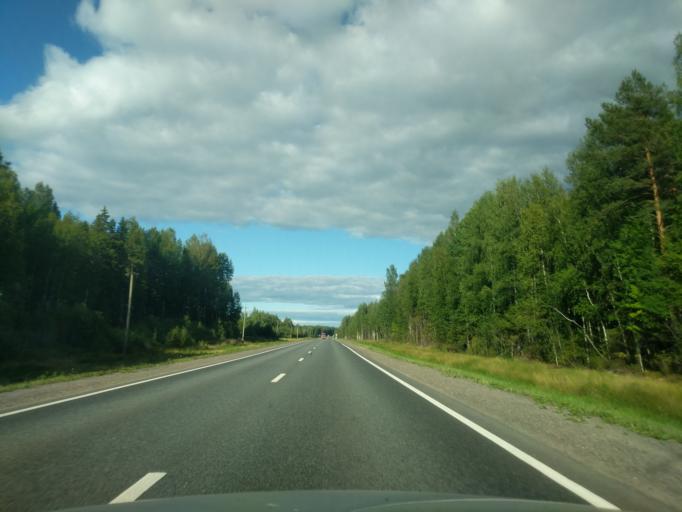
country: RU
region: Kostroma
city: Manturovo
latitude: 58.1577
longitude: 44.3875
